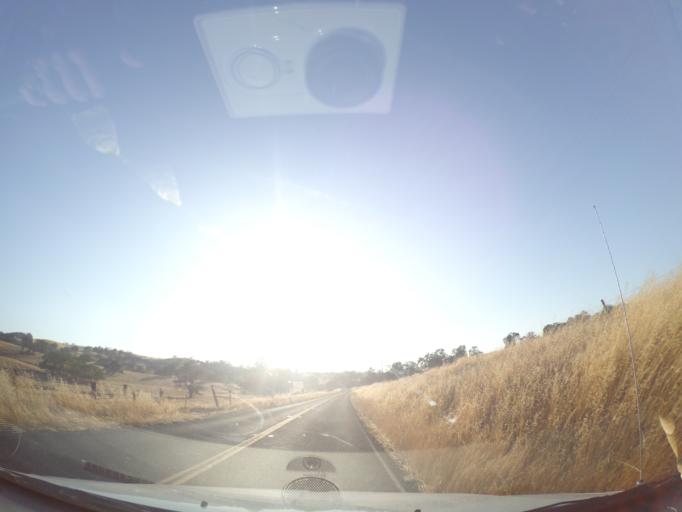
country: US
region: California
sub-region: Merced County
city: Planada
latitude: 37.4869
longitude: -120.2083
